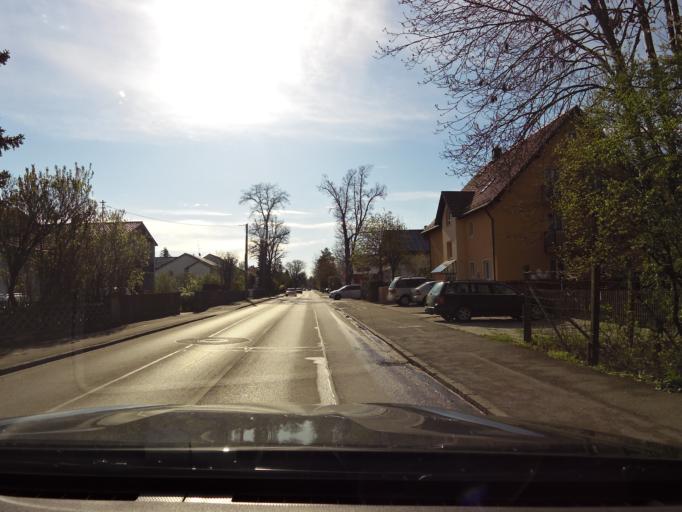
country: DE
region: Bavaria
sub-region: Upper Bavaria
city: Hallbergmoos
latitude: 48.3305
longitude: 11.7491
